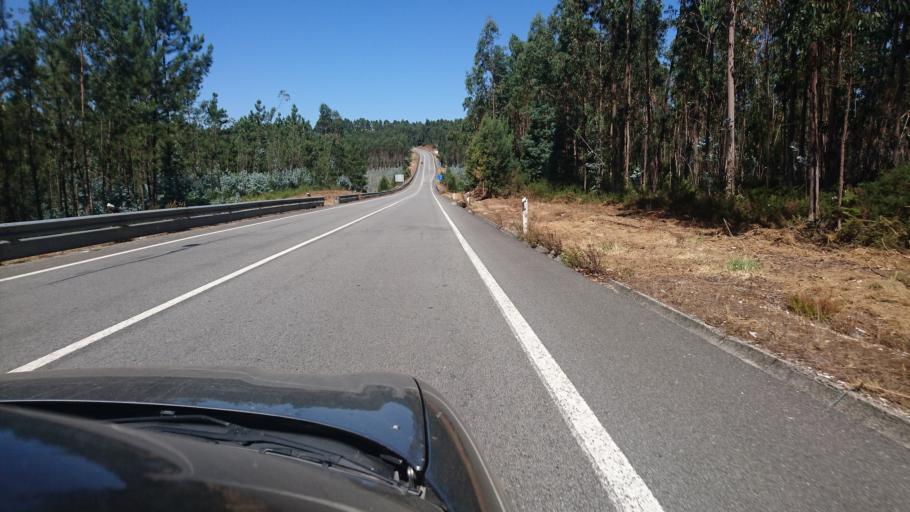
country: PT
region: Aveiro
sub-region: Santa Maria da Feira
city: Arrifana
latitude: 40.9259
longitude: -8.4918
